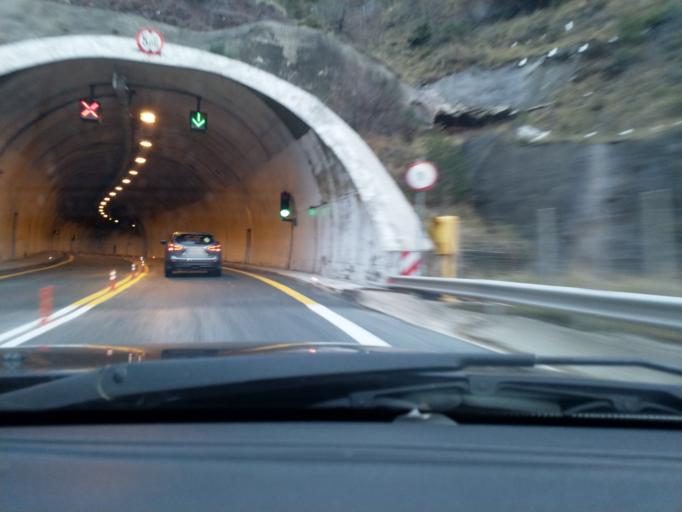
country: GR
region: Epirus
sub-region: Nomos Ioanninon
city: Metsovo
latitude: 39.7641
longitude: 21.1694
